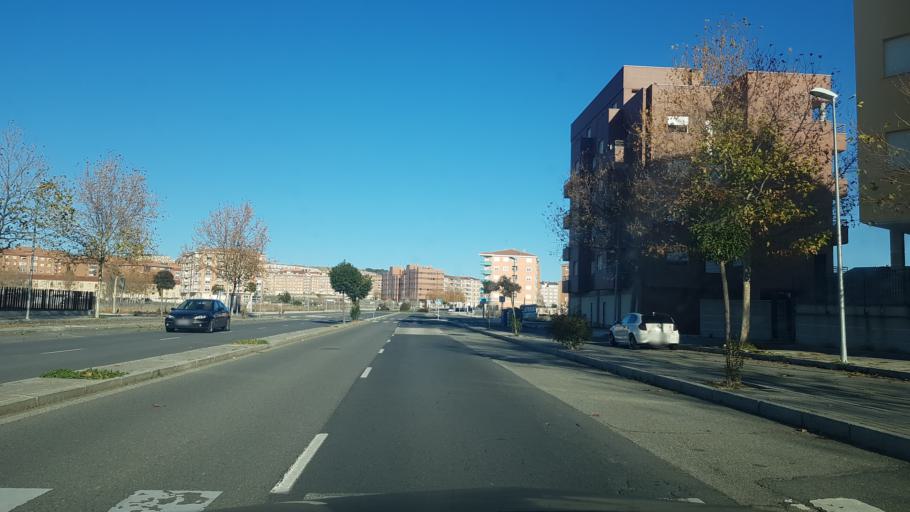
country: ES
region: Castille and Leon
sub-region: Provincia de Avila
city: Avila
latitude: 40.6429
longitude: -4.6862
